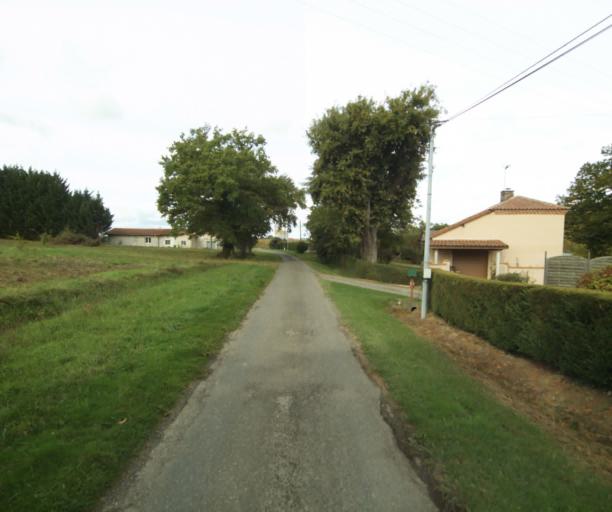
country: FR
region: Midi-Pyrenees
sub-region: Departement du Gers
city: Eauze
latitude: 43.8372
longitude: 0.0975
